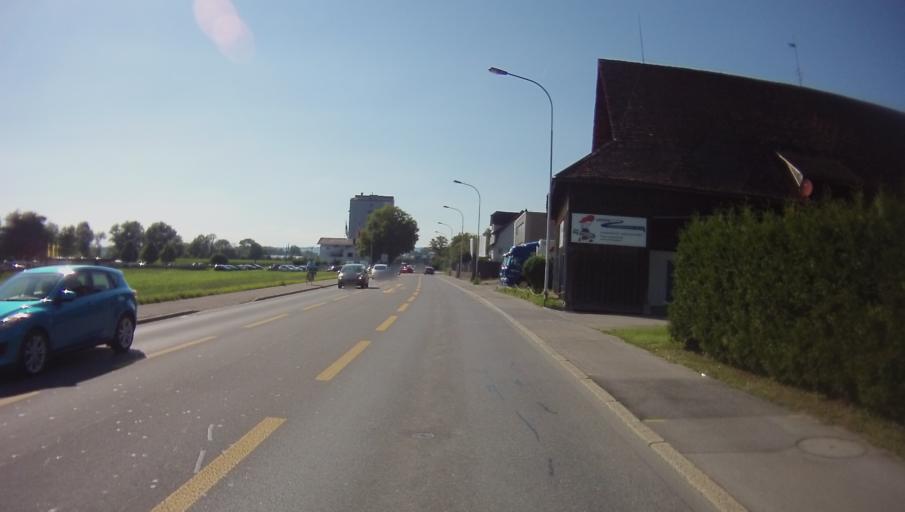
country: CH
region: Zug
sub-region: Zug
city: Steinhausen
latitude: 47.1781
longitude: 8.4965
